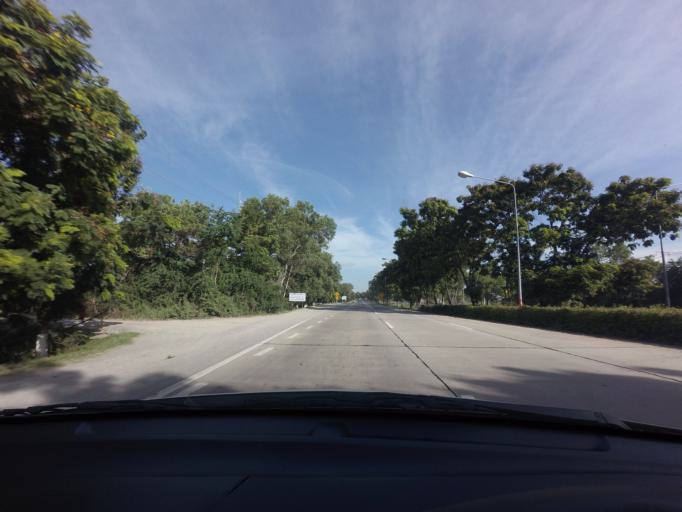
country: TH
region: Suphan Buri
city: Bang Pla Ma
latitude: 14.3475
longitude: 100.1891
